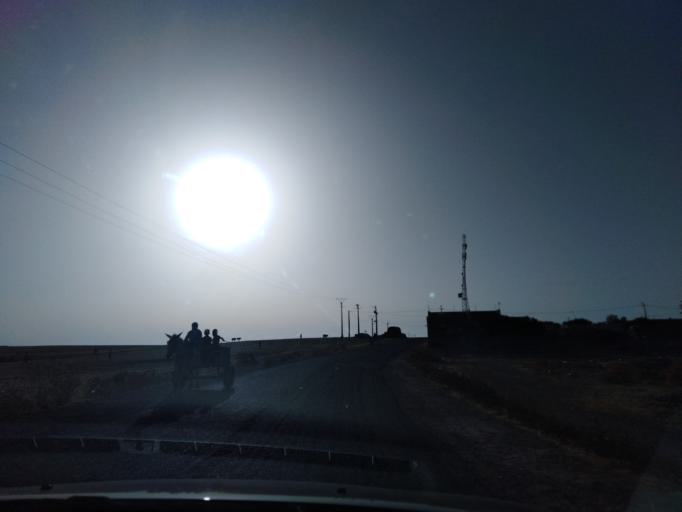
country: MA
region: Doukkala-Abda
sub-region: Safi
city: Safi
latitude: 32.4867
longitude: -8.9184
